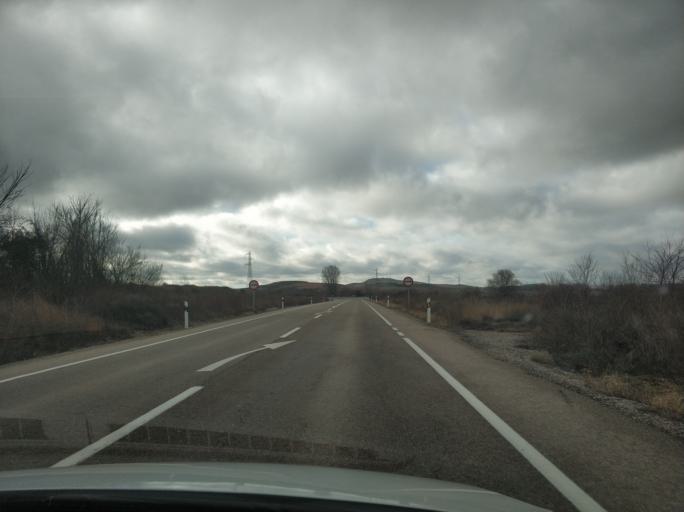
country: ES
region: Castille and Leon
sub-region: Provincia de Soria
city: San Esteban de Gormaz
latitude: 41.5664
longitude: -3.2399
